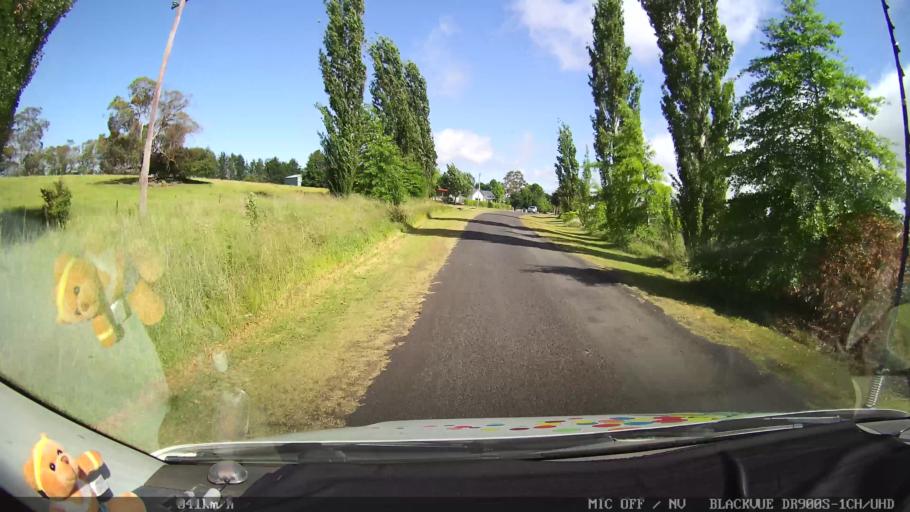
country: AU
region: New South Wales
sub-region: Guyra
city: Guyra
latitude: -30.0241
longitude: 151.6606
